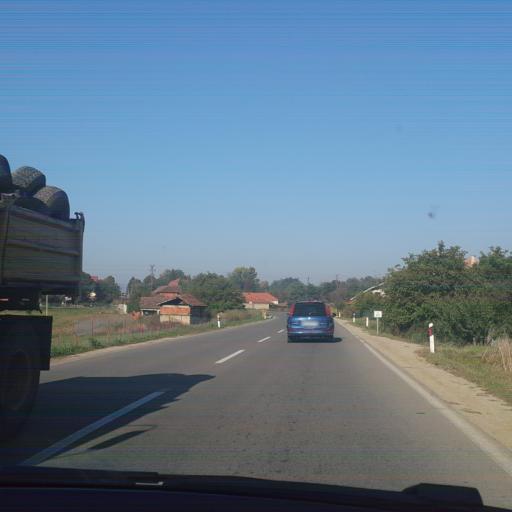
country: RS
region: Central Serbia
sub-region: Toplicki Okrug
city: Prokuplje
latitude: 43.2412
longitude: 21.4889
